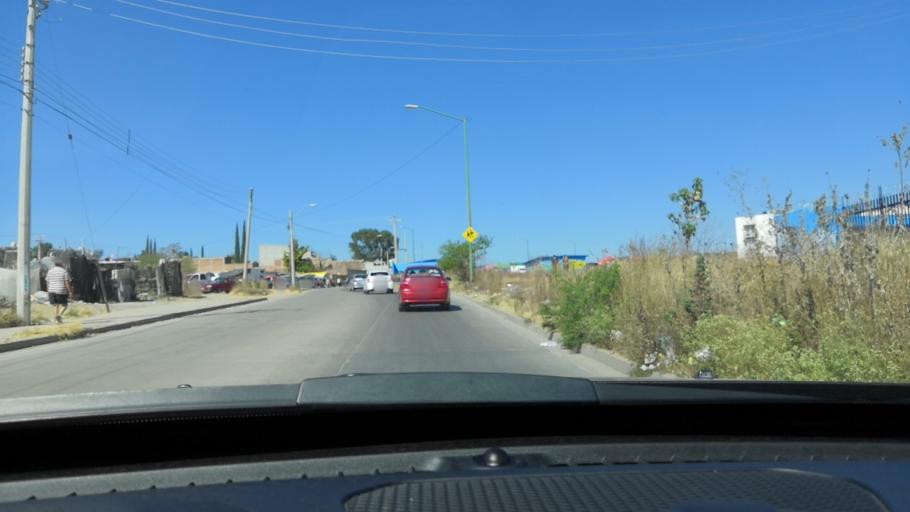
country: MX
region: Guanajuato
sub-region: Leon
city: Centro Familiar la Soledad
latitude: 21.1412
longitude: -101.7513
